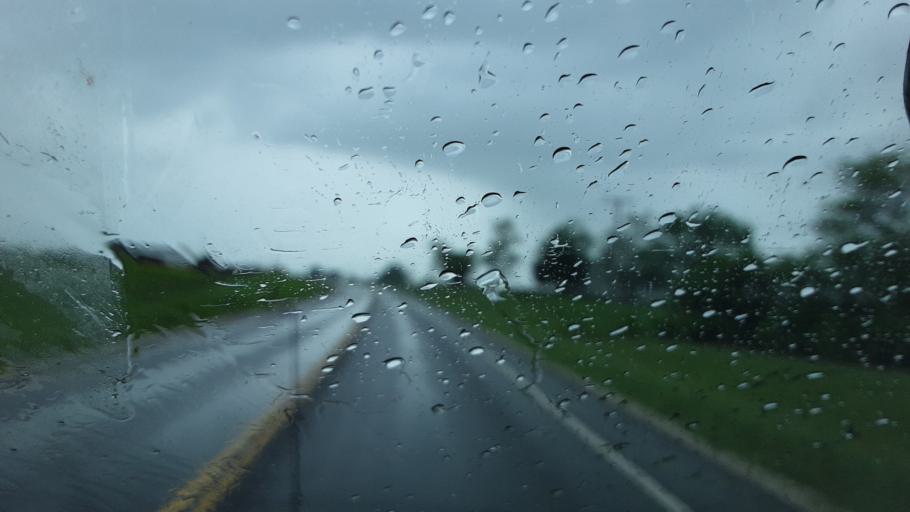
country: US
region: Missouri
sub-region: Monroe County
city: Paris
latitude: 39.4796
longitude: -92.1768
